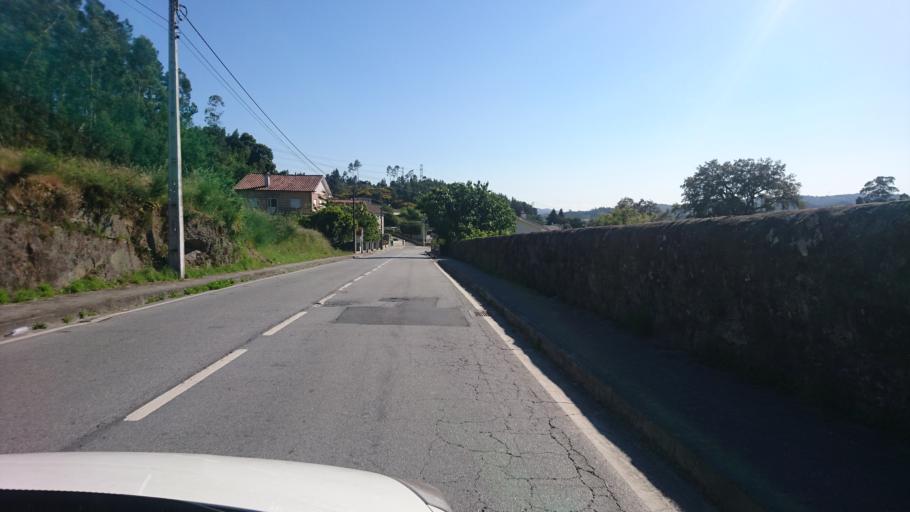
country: PT
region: Porto
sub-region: Paredes
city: Paredes
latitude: 41.1913
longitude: -8.3256
